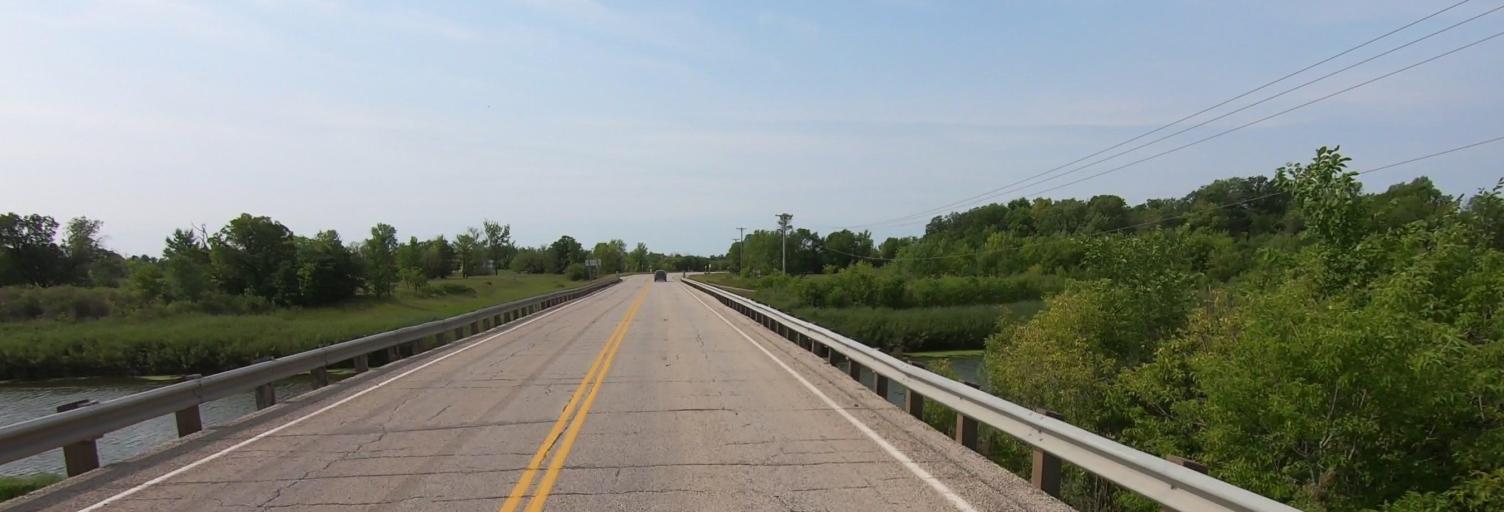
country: CA
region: Manitoba
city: Niverville
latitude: 49.6971
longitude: -97.0976
